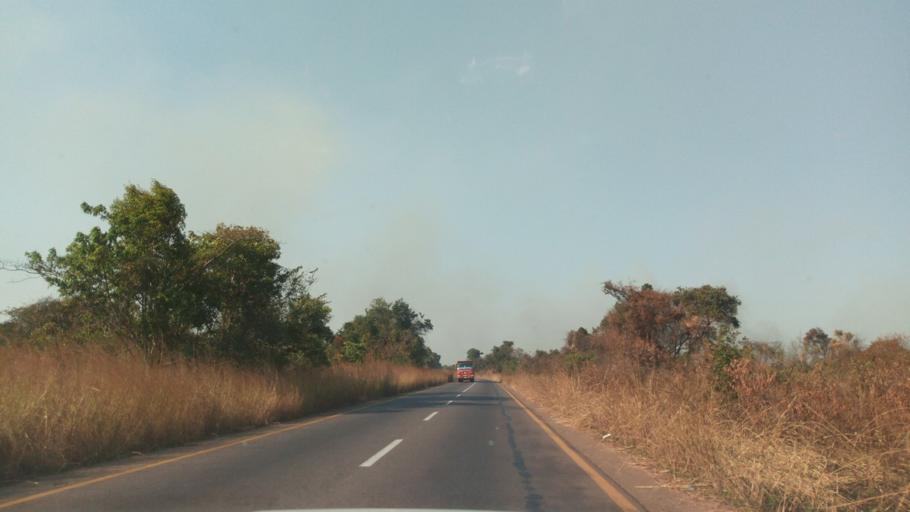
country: CD
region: Katanga
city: Lubumbashi
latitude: -11.4189
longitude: 27.7350
